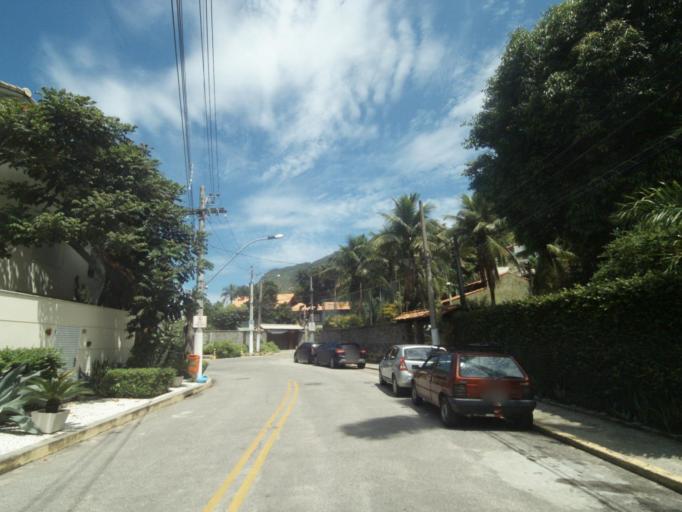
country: BR
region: Rio de Janeiro
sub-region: Niteroi
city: Niteroi
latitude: -22.9733
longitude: -43.0384
